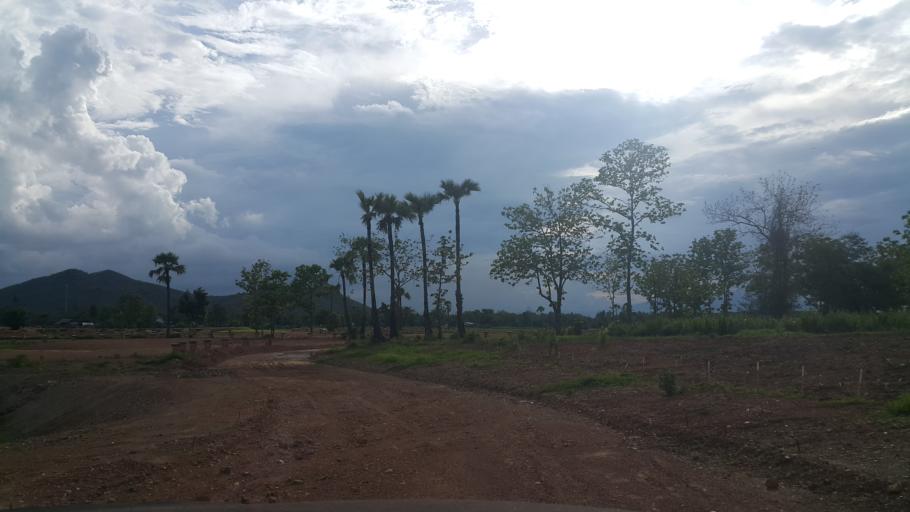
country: TH
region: Chiang Mai
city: Mae On
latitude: 18.7223
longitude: 99.2168
